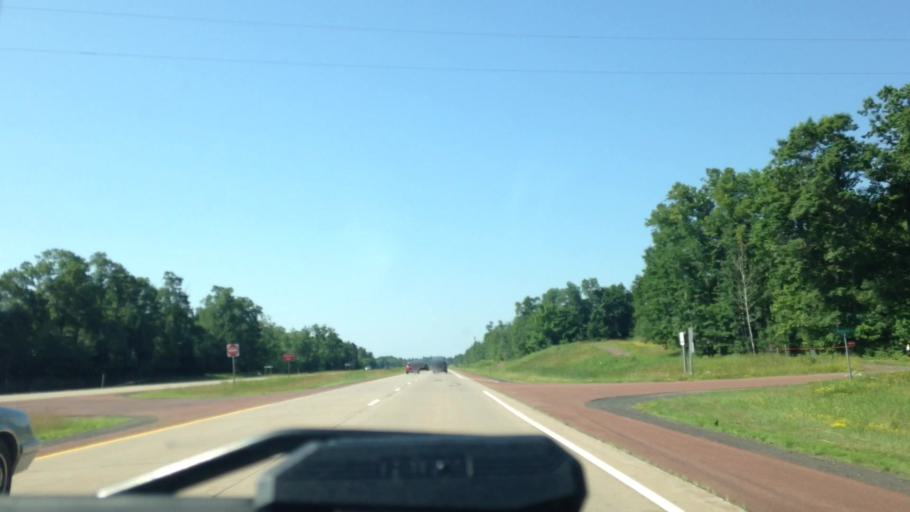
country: US
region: Wisconsin
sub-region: Douglas County
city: Lake Nebagamon
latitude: 46.3749
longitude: -91.8260
